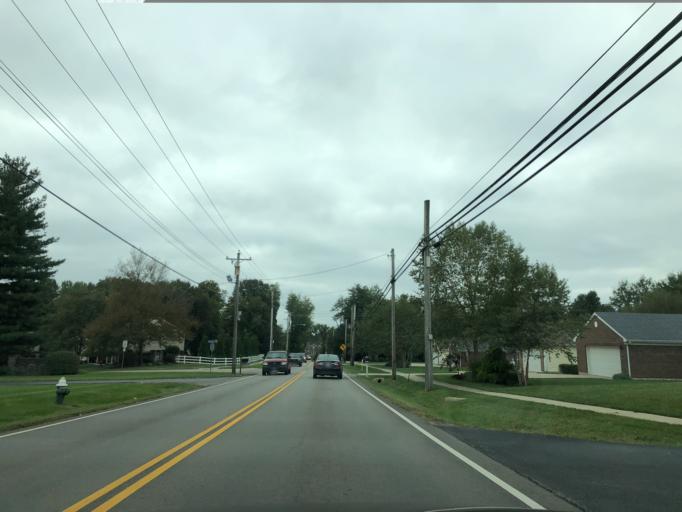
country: US
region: Ohio
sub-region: Hamilton County
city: Loveland
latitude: 39.2821
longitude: -84.2841
